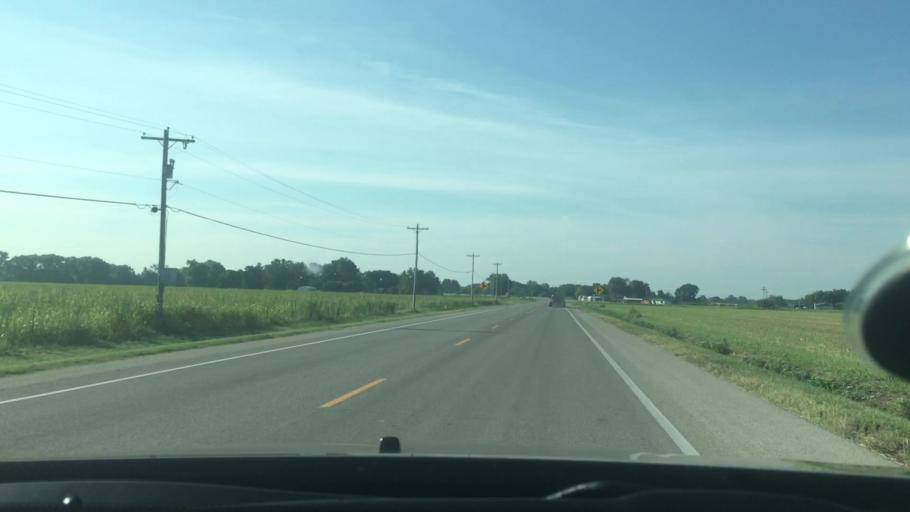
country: US
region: Oklahoma
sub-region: Garvin County
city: Wynnewood
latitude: 34.6564
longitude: -97.2020
